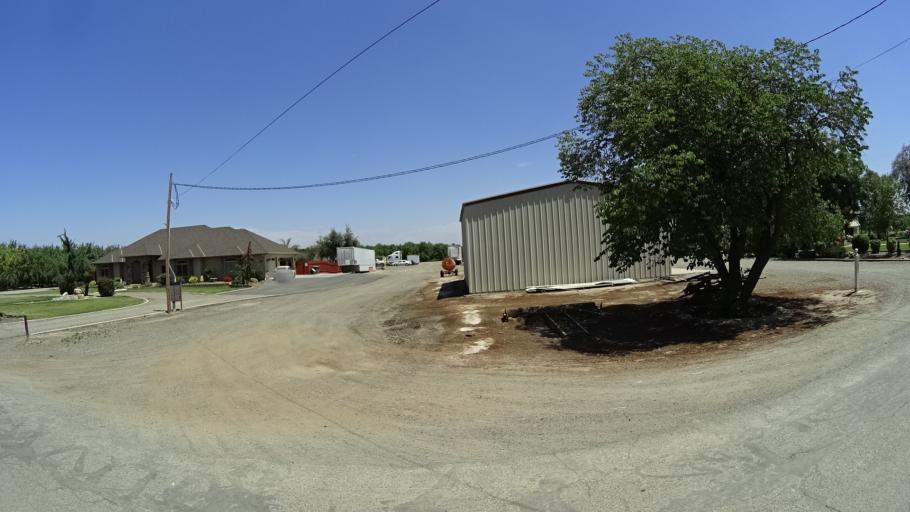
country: US
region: California
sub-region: Kings County
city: Lucerne
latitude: 36.4121
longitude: -119.6190
